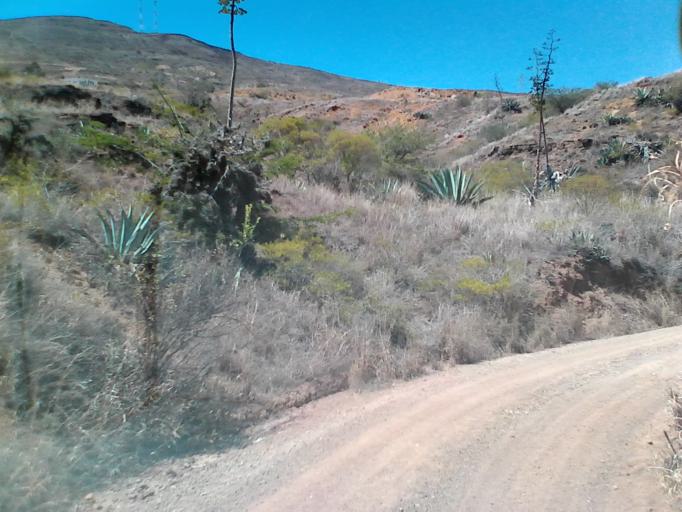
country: CO
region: Boyaca
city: Sachica
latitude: 5.5904
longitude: -73.5684
